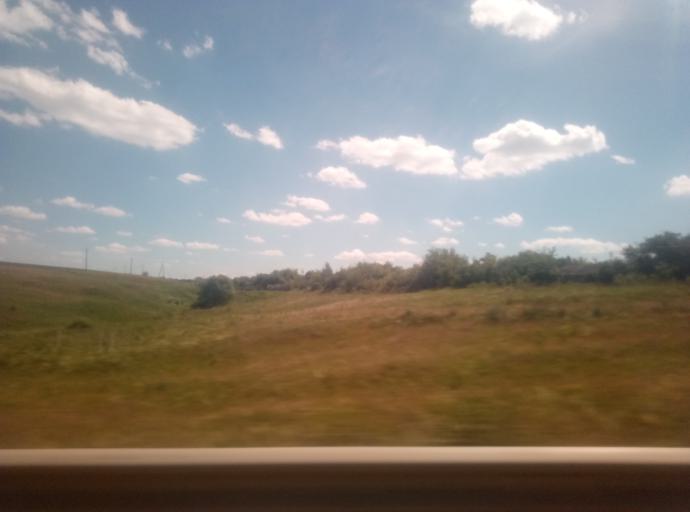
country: RU
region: Tula
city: Kireyevsk
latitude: 53.9382
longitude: 37.9474
